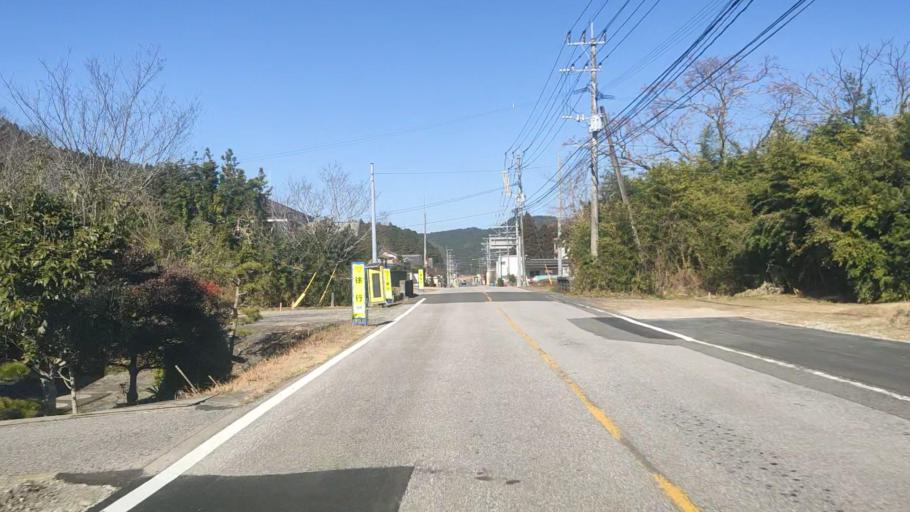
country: JP
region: Oita
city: Saiki
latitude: 32.9183
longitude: 131.9280
